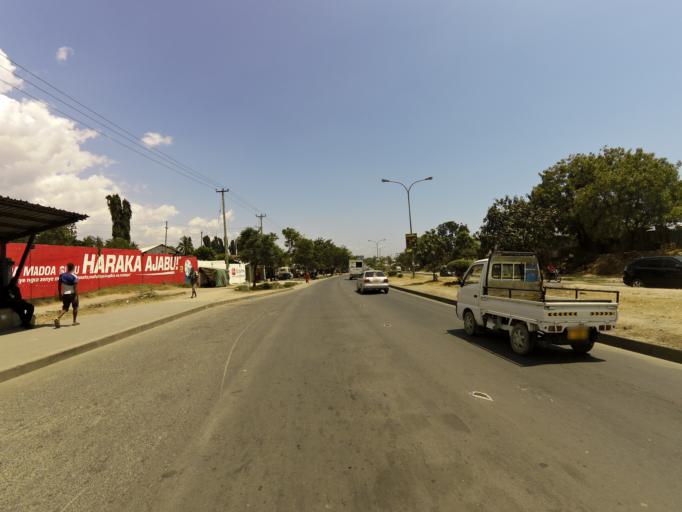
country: TZ
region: Dar es Salaam
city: Dar es Salaam
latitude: -6.8222
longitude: 39.2583
